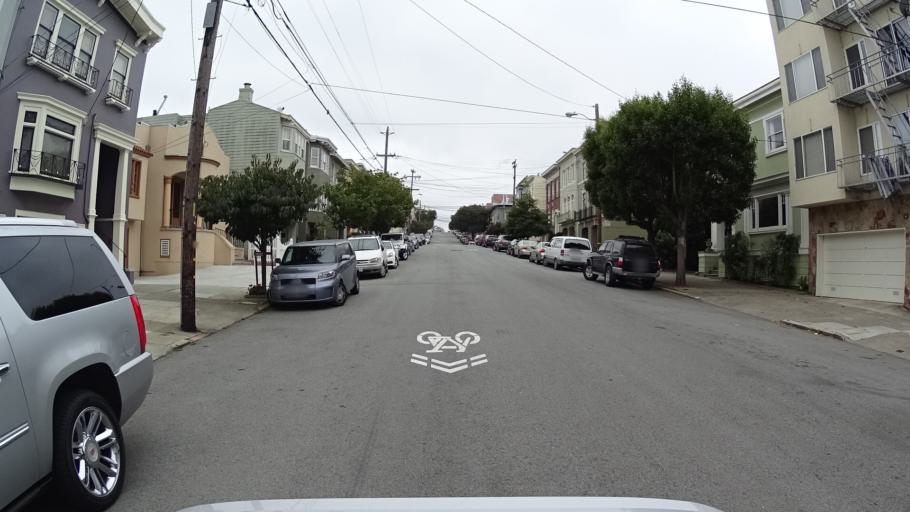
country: US
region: California
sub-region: San Francisco County
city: San Francisco
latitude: 37.7795
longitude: -122.4739
